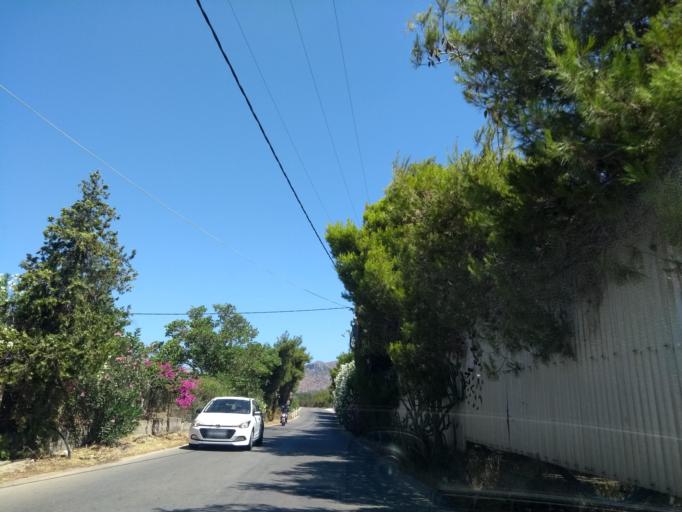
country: GR
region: Crete
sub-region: Nomos Chanias
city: Mouzouras
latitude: 35.5451
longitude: 24.1288
